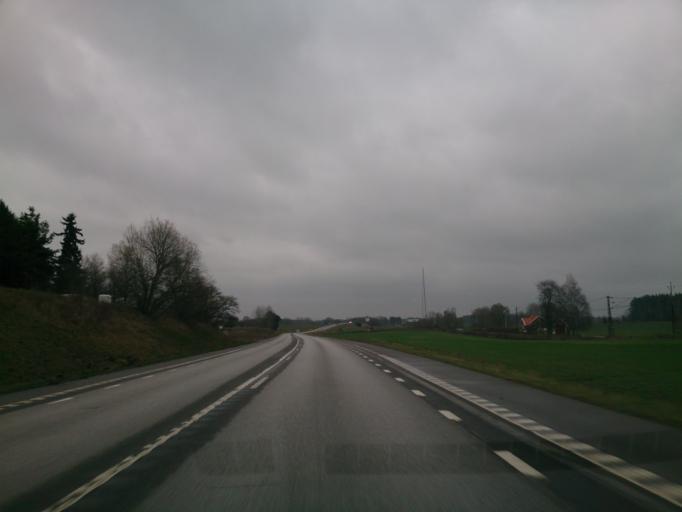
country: SE
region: OEstergoetland
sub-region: Linkopings Kommun
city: Linghem
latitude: 58.4596
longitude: 15.8678
